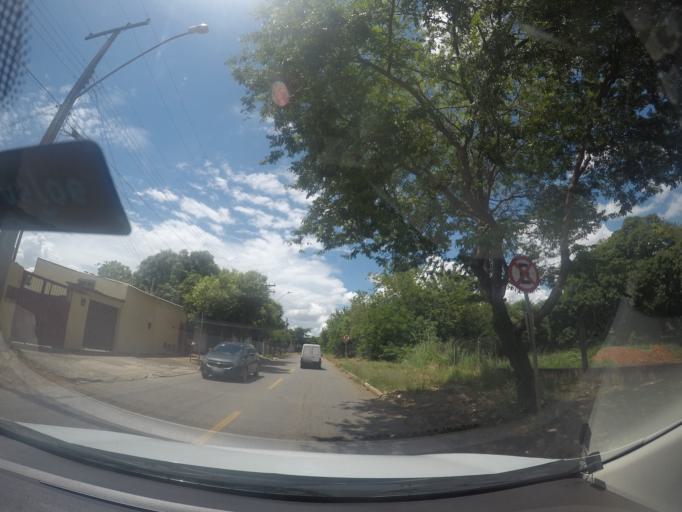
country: BR
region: Goias
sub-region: Goiania
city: Goiania
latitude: -16.7130
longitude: -49.3168
